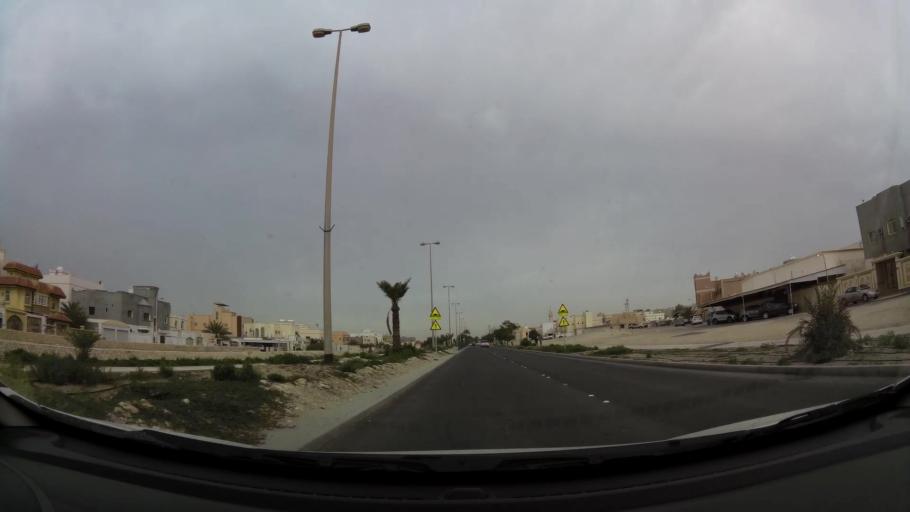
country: BH
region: Central Governorate
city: Dar Kulayb
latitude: 26.0645
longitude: 50.5078
